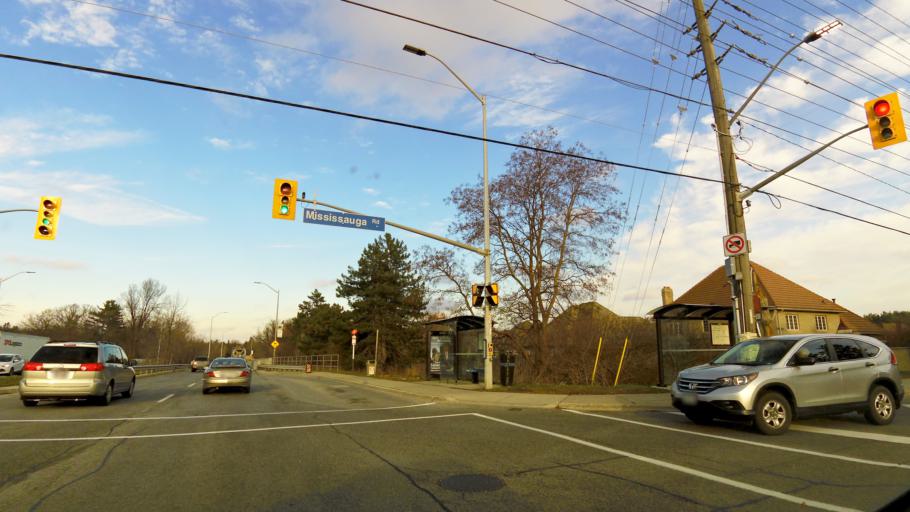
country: CA
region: Ontario
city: Mississauga
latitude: 43.5530
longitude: -79.6755
